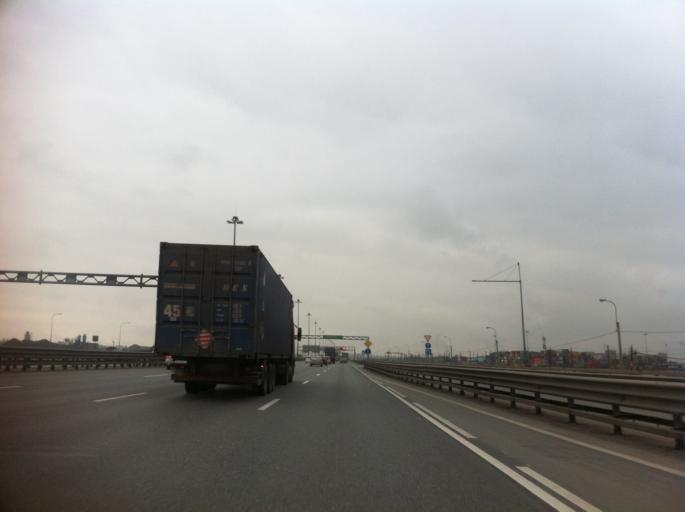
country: RU
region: St.-Petersburg
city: Kupchino
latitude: 59.8148
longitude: 30.3145
